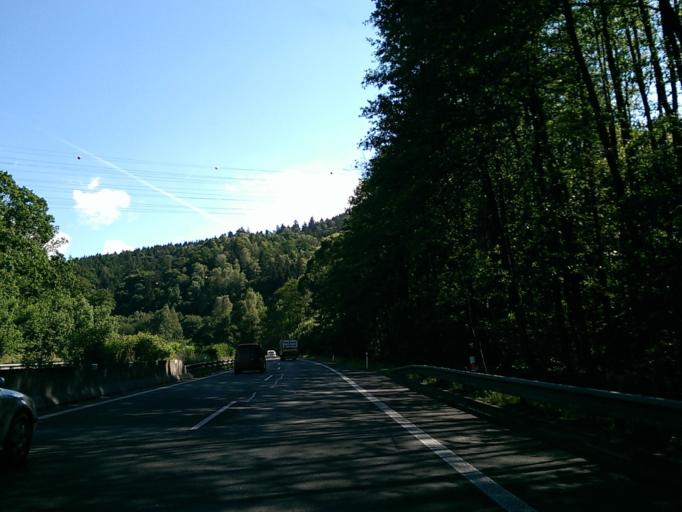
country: CZ
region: Liberecky
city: Hodkovice nad Mohelkou
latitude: 50.6759
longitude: 15.0994
